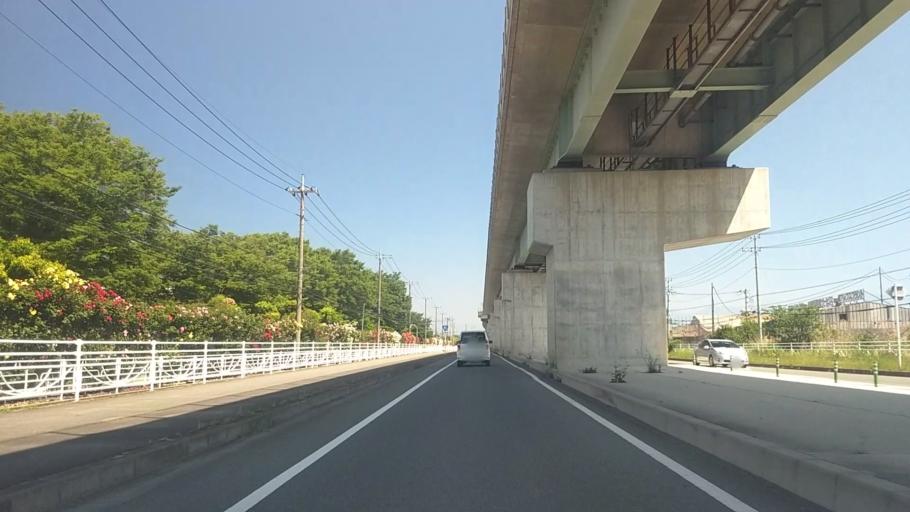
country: JP
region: Yamanashi
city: Ryuo
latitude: 35.5786
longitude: 138.4753
